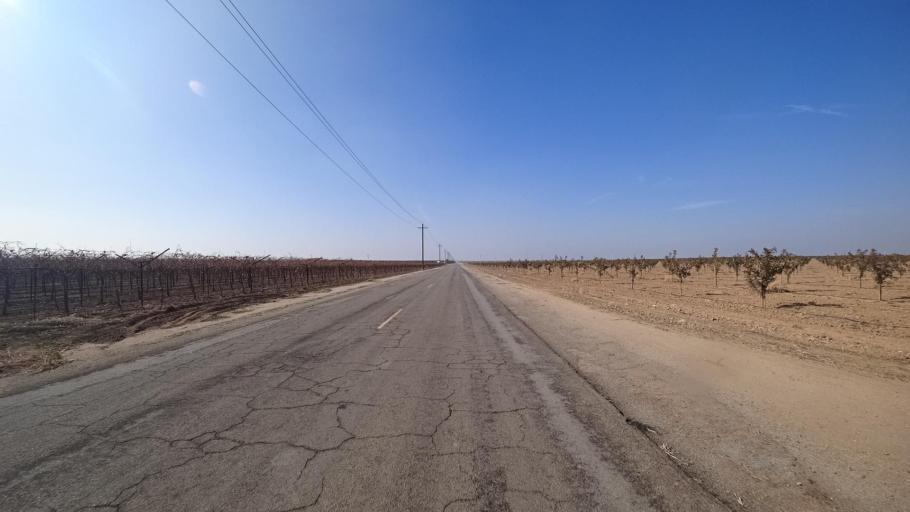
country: US
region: California
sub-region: Kern County
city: Shafter
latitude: 35.5299
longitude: -119.1296
